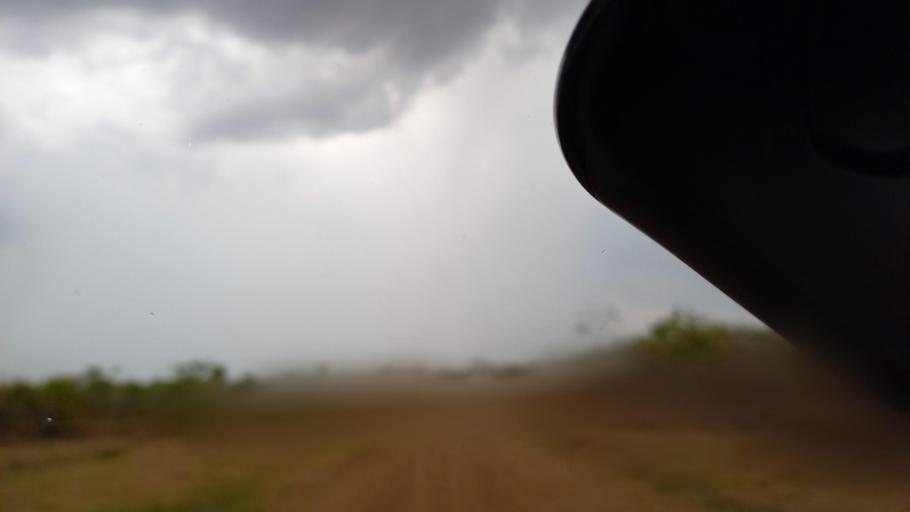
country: ZM
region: Lusaka
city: Kafue
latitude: -15.8678
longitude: 28.1892
